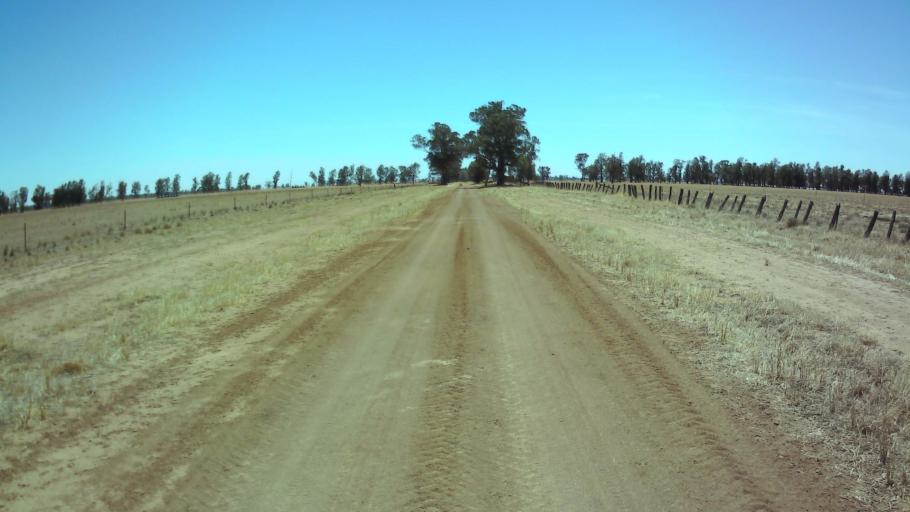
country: AU
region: New South Wales
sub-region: Weddin
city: Grenfell
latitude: -33.9730
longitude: 147.7377
